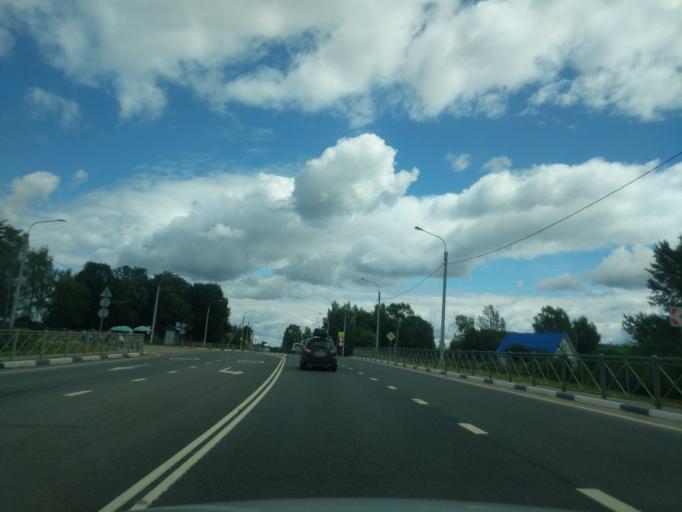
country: RU
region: Jaroslavl
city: Levashevo
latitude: 57.6428
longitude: 40.5264
